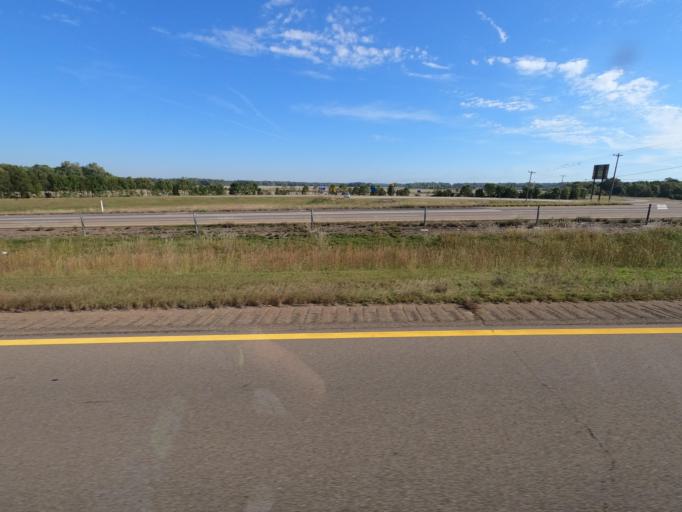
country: US
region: Tennessee
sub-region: Shelby County
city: Arlington
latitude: 35.2899
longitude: -89.6877
